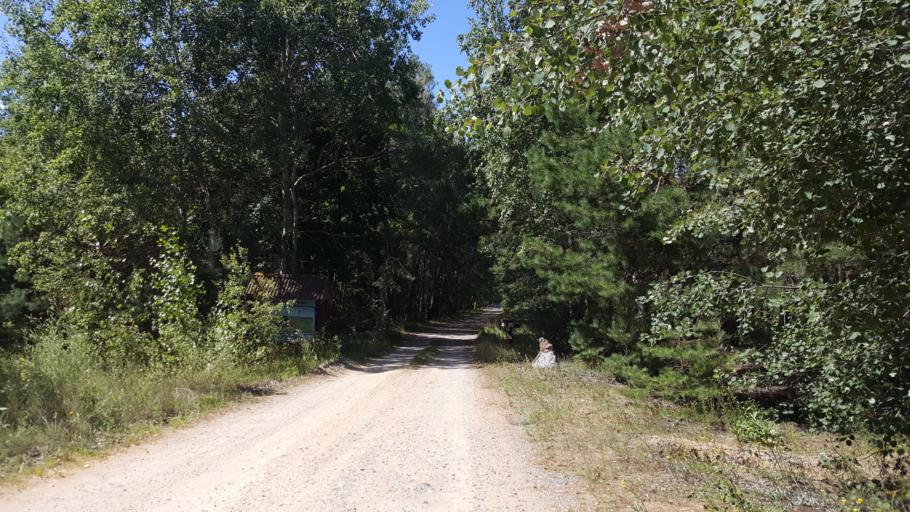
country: BY
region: Brest
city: Kobryn
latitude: 52.3490
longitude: 24.3249
